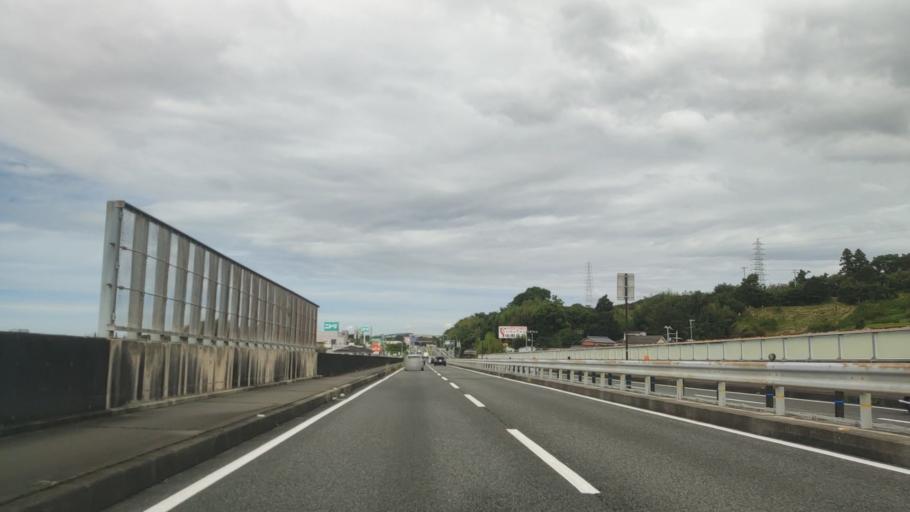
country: JP
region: Wakayama
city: Tanabe
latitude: 33.7185
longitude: 135.4071
